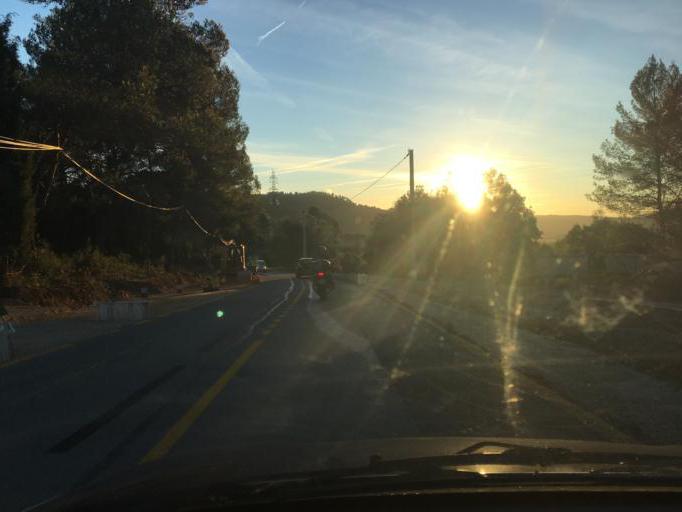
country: FR
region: Provence-Alpes-Cote d'Azur
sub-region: Departement du Var
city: Taradeau
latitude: 43.4602
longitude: 6.4165
